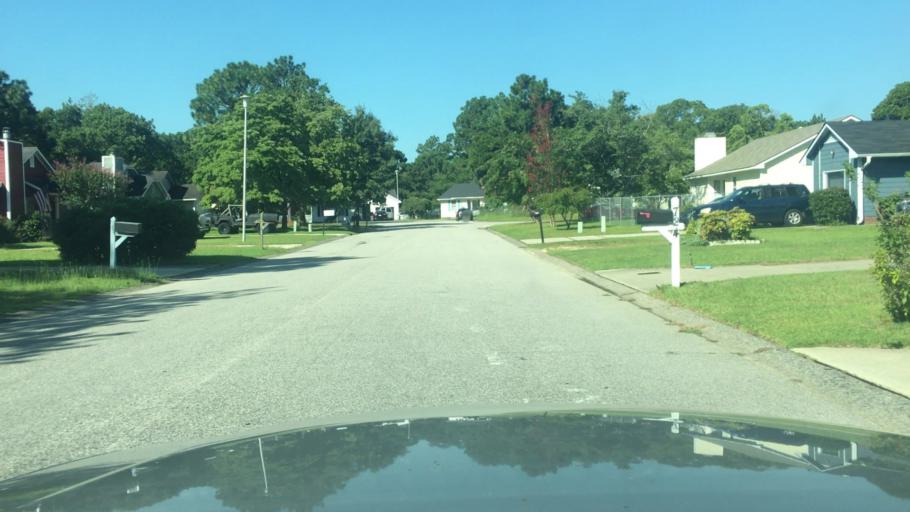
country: US
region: North Carolina
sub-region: Cumberland County
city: Spring Lake
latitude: 35.1306
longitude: -78.9051
